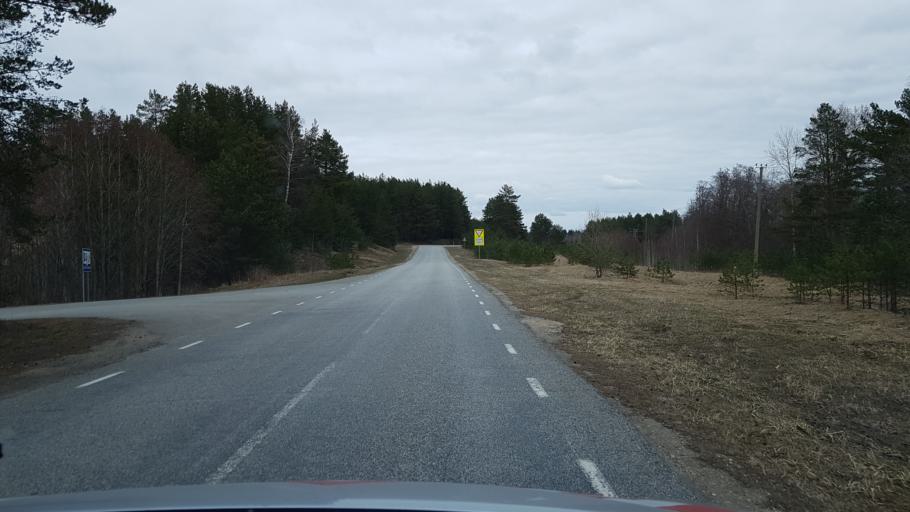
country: EE
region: Ida-Virumaa
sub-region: Narva linn
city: Narva
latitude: 59.4271
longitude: 28.1210
